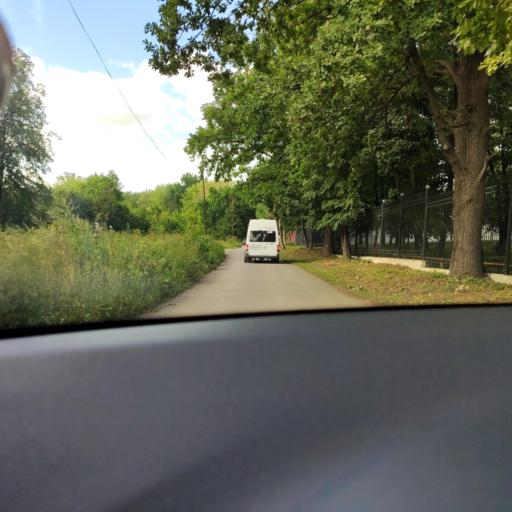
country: RU
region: Samara
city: Novosemeykino
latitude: 53.3498
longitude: 50.2443
